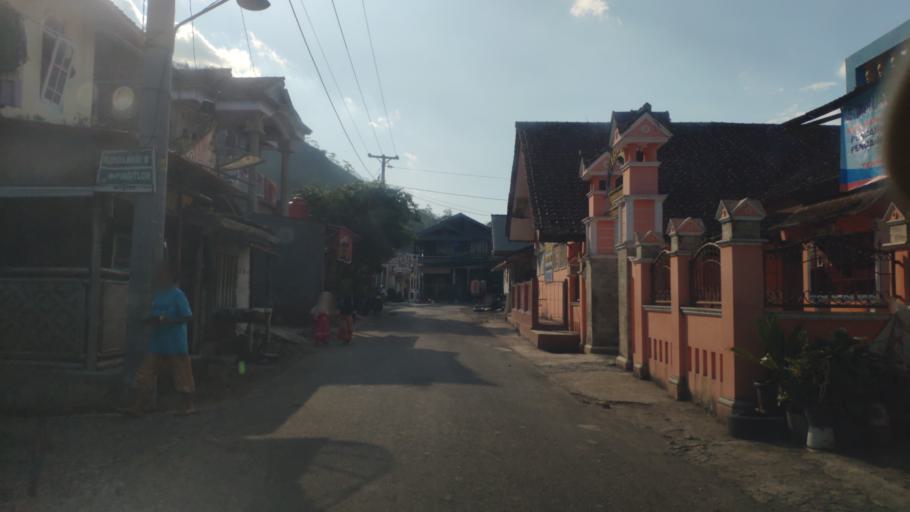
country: ID
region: Central Java
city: Buaran
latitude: -7.2421
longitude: 109.5824
